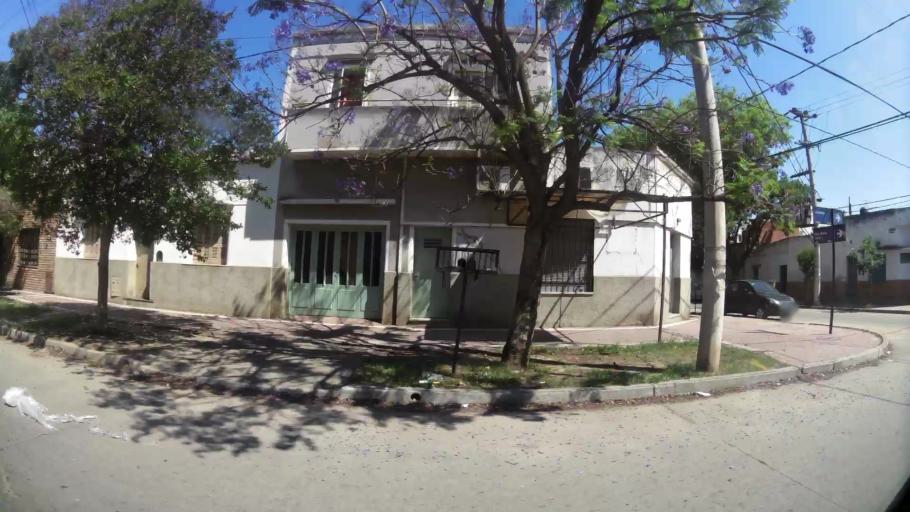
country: AR
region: Cordoba
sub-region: Departamento de Capital
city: Cordoba
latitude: -31.4050
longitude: -64.1630
